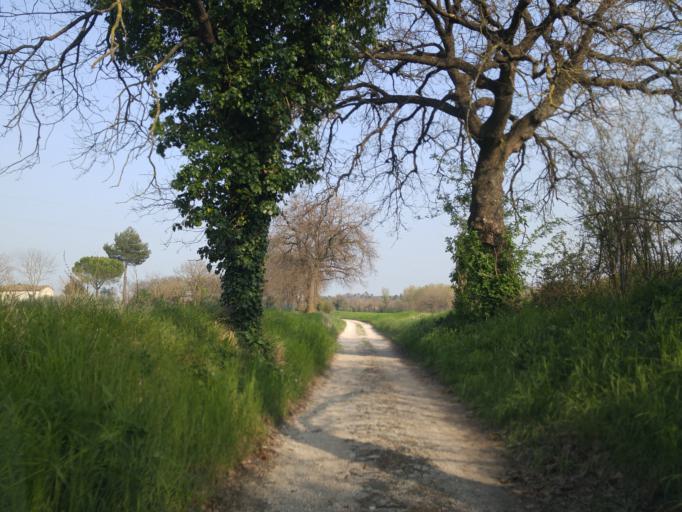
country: IT
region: The Marches
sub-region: Provincia di Pesaro e Urbino
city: Sant'Ippolito
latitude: 43.7035
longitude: 12.8526
